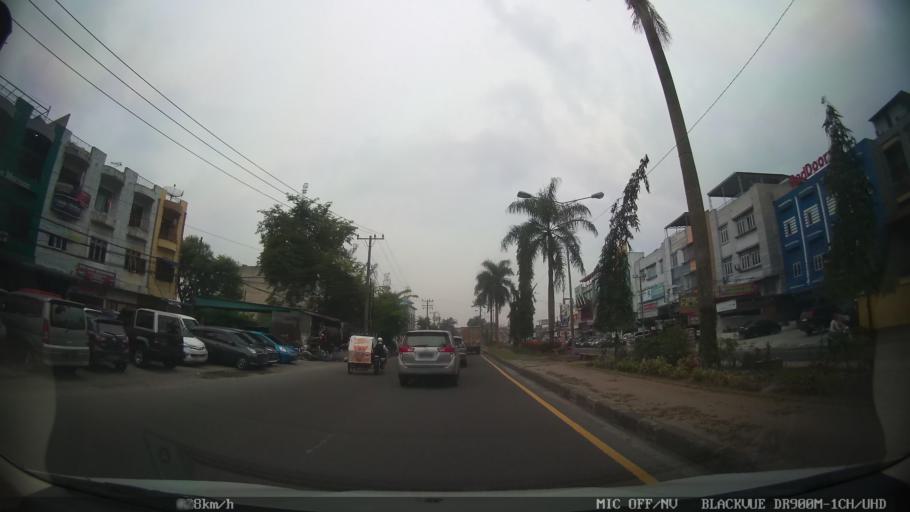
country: ID
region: North Sumatra
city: Deli Tua
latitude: 3.5381
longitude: 98.6919
